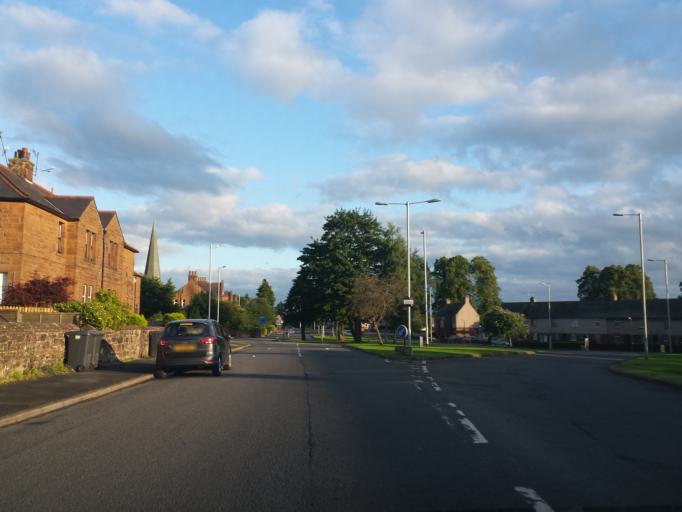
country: GB
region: Scotland
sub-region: Dumfries and Galloway
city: Dumfries
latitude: 55.0740
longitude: -3.6220
